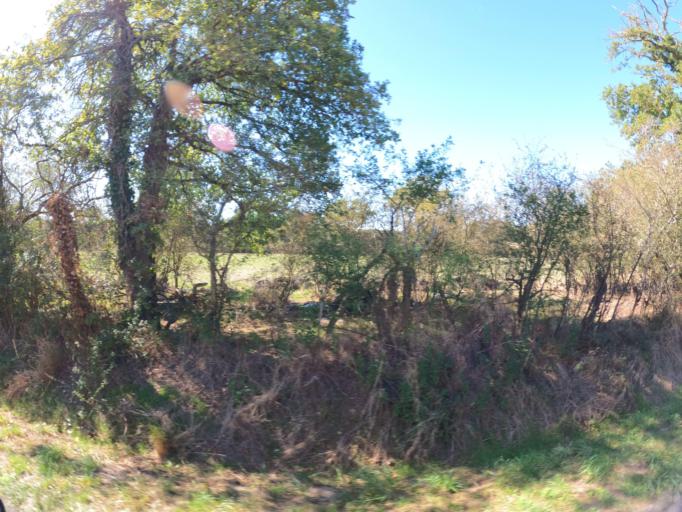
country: FR
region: Poitou-Charentes
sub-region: Departement de la Vienne
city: Lathus-Saint-Remy
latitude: 46.2872
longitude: 1.0063
